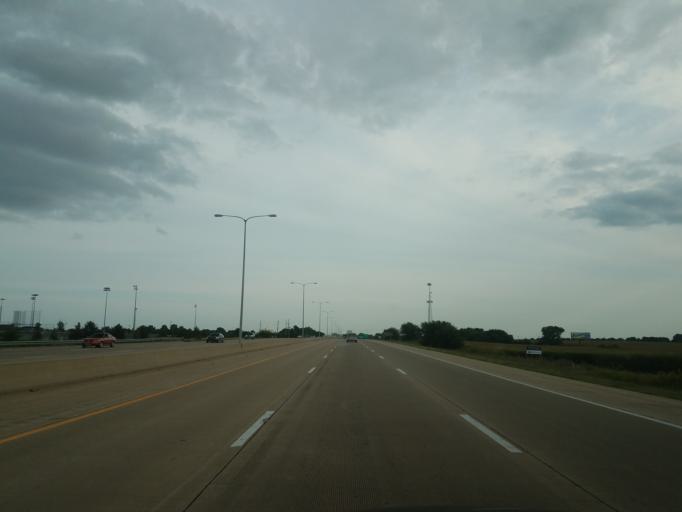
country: US
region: Illinois
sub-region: McLean County
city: Normal
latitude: 40.5216
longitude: -89.0282
